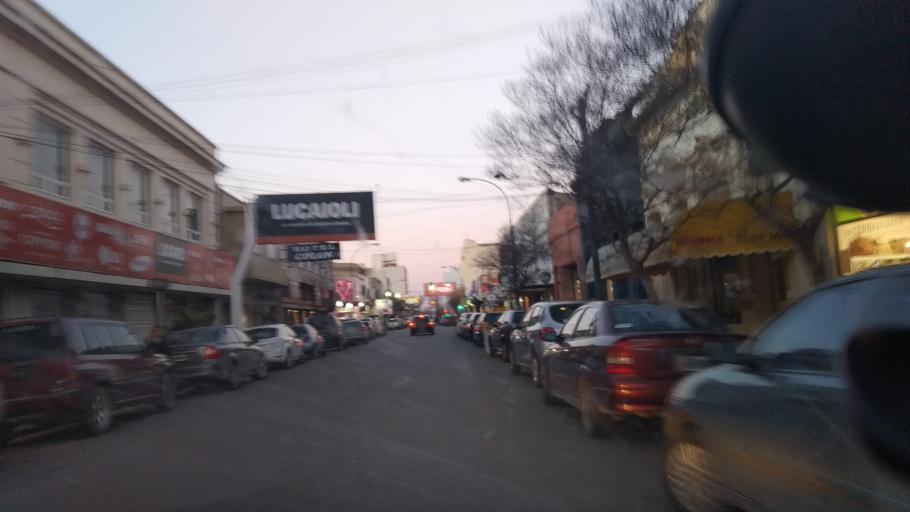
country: AR
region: Buenos Aires
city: Necochea
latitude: -38.5543
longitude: -58.7431
